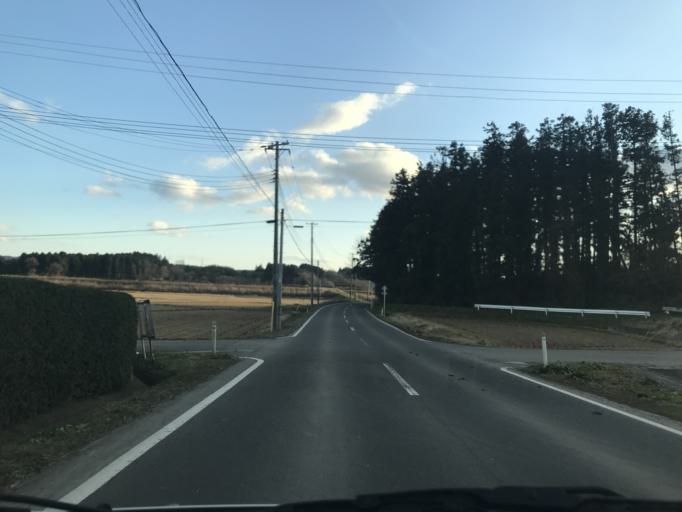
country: JP
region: Miyagi
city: Kogota
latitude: 38.6346
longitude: 141.0697
